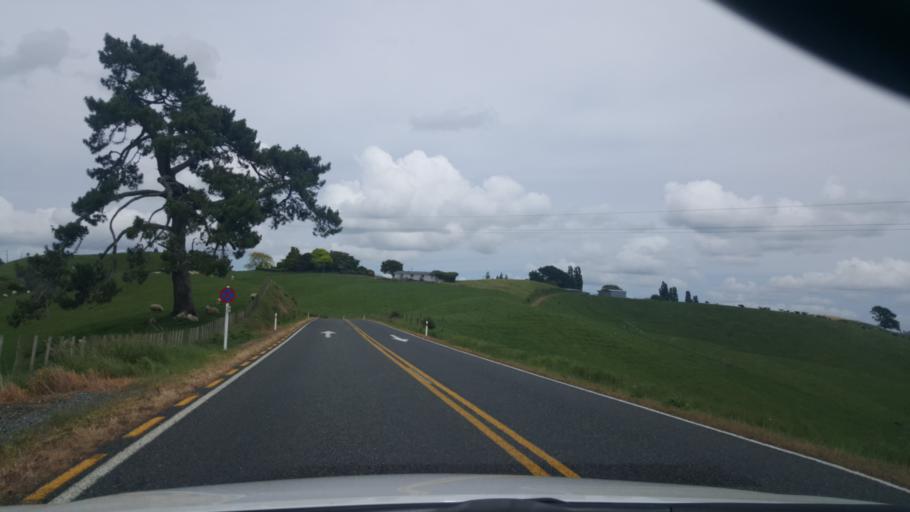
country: NZ
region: Waikato
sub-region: Matamata-Piako District
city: Matamata
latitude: -37.8746
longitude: 175.6855
